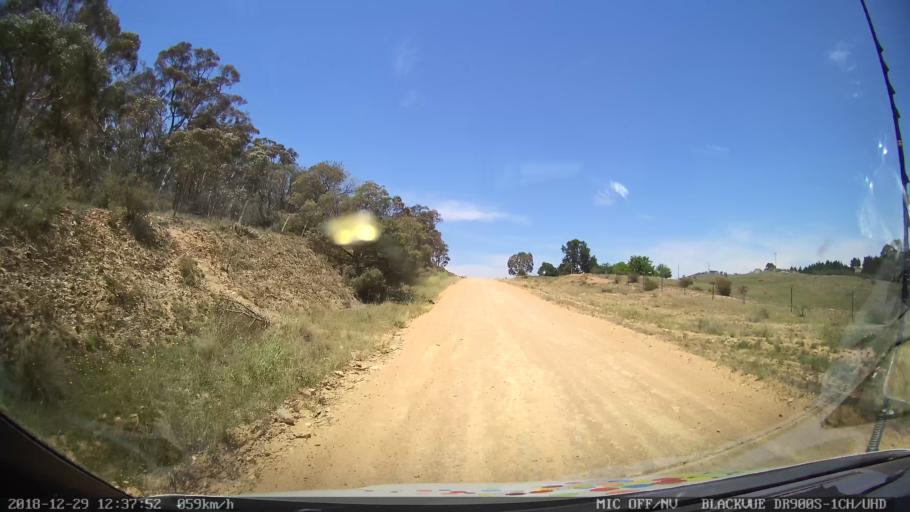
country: AU
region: Australian Capital Territory
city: Macarthur
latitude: -35.5841
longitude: 149.2290
